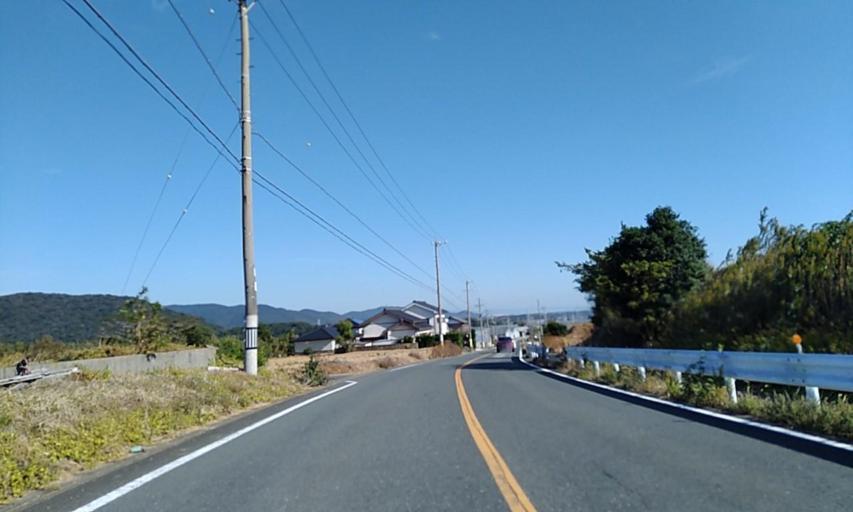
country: JP
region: Aichi
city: Tahara
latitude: 34.6243
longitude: 137.2286
